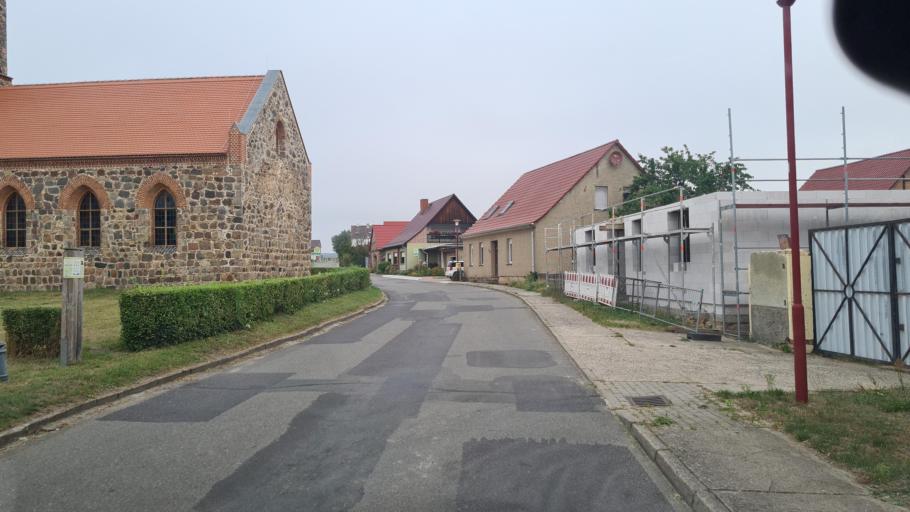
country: DE
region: Brandenburg
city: Niemegk
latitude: 52.0721
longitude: 12.6198
